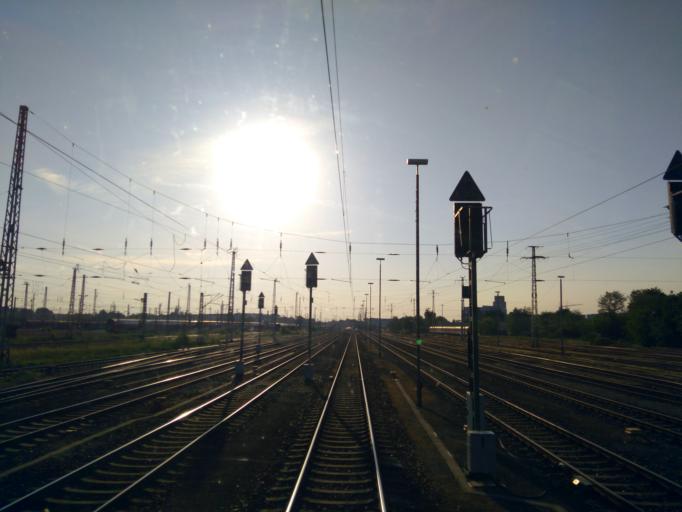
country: DE
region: Brandenburg
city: Cottbus
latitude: 51.7502
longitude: 14.3149
